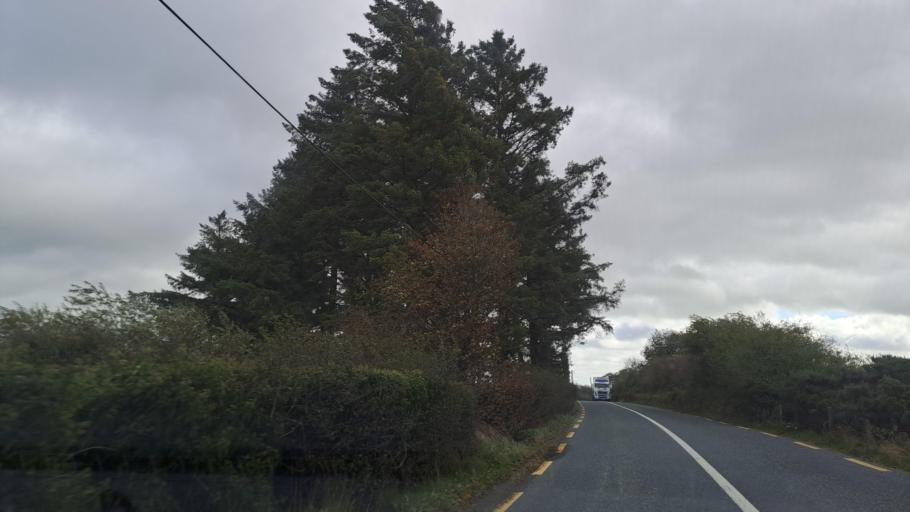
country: IE
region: Ulster
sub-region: An Cabhan
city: Kingscourt
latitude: 53.9248
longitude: -6.8719
